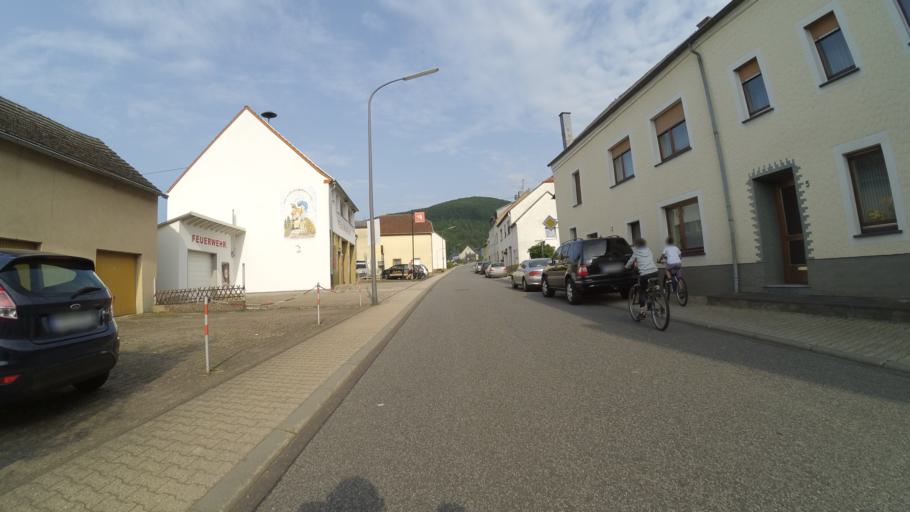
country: DE
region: Rheinland-Pfalz
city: Irsch
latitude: 49.6040
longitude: 6.5948
